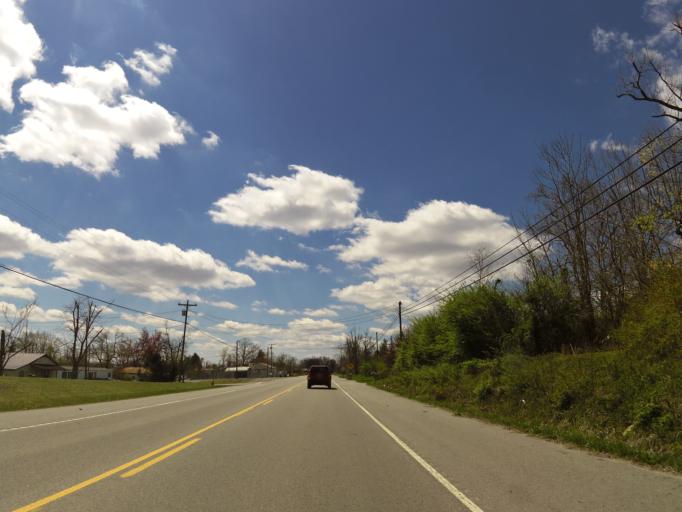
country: US
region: Tennessee
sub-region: White County
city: Sparta
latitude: 35.9499
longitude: -85.3096
